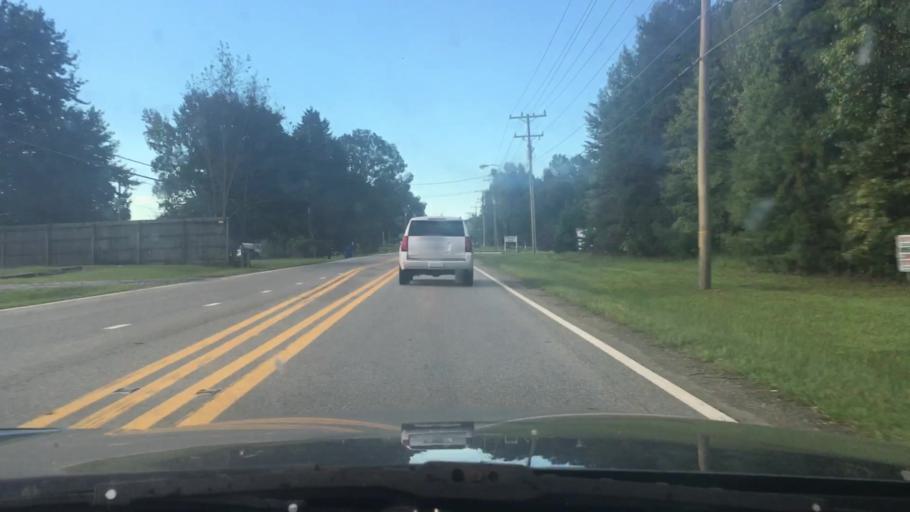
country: US
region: North Carolina
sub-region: Alamance County
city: Green Level
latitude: 36.1378
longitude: -79.3449
